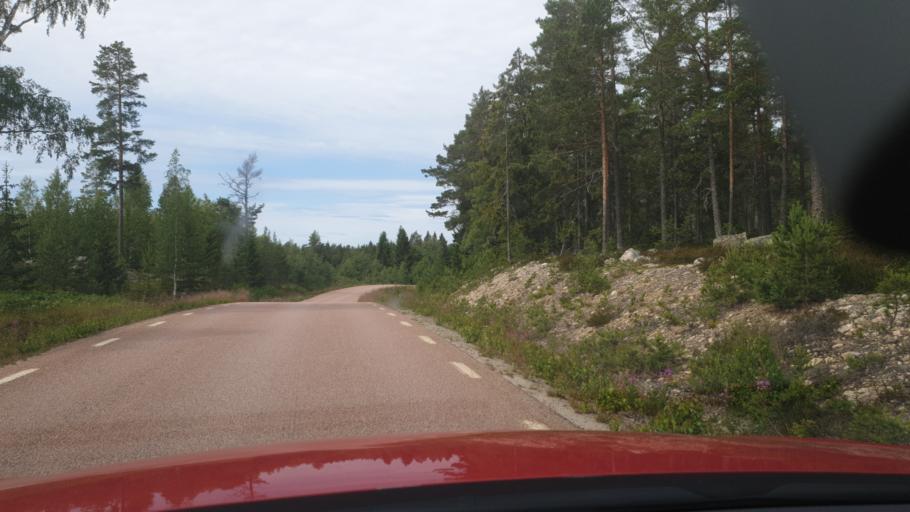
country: SE
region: Gaevleborg
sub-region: Hudiksvalls Kommun
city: Hudiksvall
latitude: 61.7017
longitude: 17.4835
